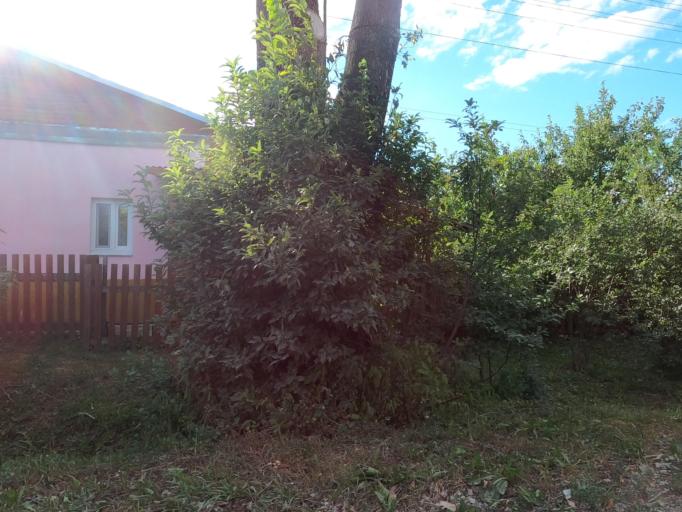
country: RU
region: Moskovskaya
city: Konobeyevo
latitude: 55.4105
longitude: 38.7185
